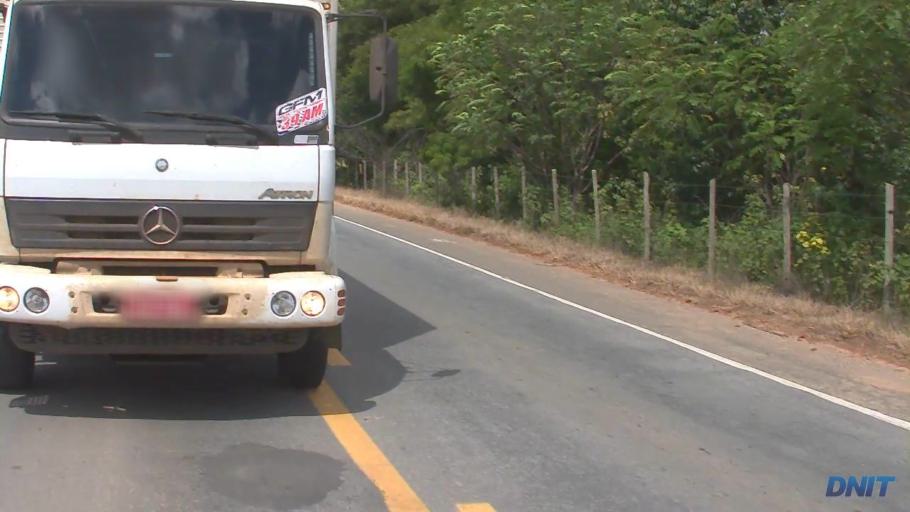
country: BR
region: Minas Gerais
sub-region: Governador Valadares
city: Governador Valadares
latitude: -19.0503
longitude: -42.1577
